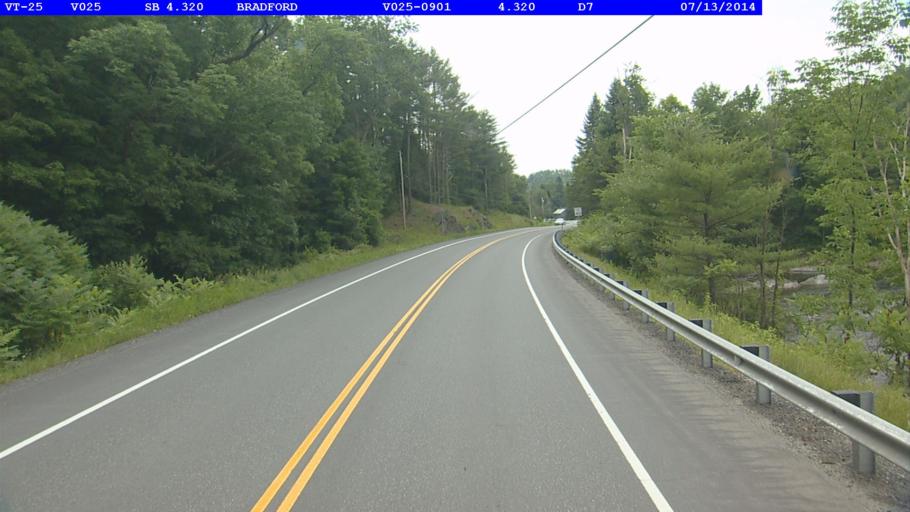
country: US
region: New Hampshire
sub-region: Grafton County
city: Haverhill
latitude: 44.0153
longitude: -72.1708
